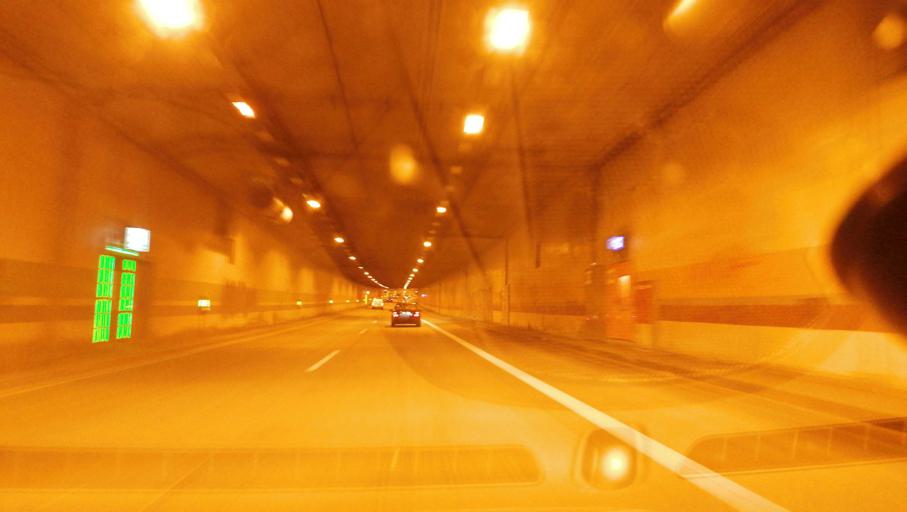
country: DE
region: North Rhine-Westphalia
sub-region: Regierungsbezirk Arnsberg
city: Dortmund
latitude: 51.5201
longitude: 7.5183
